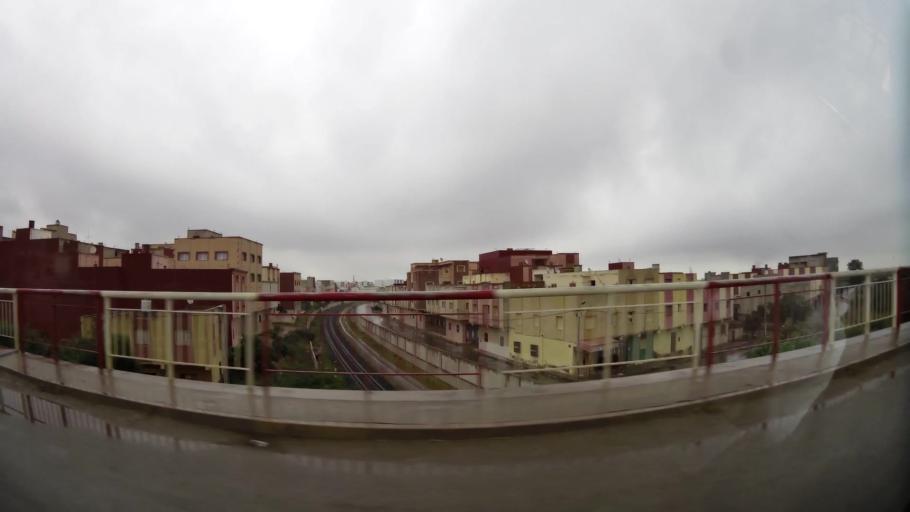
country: MA
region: Oriental
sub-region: Nador
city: Nador
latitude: 35.1537
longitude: -2.9758
